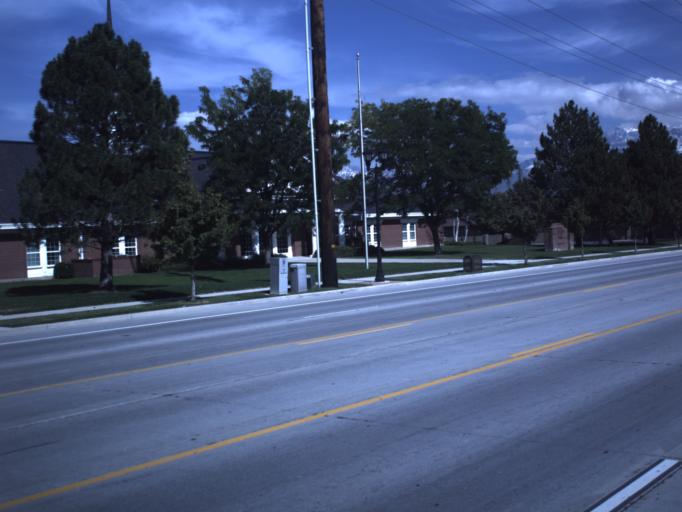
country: US
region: Utah
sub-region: Salt Lake County
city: South Jordan Heights
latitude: 40.5441
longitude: -111.9448
